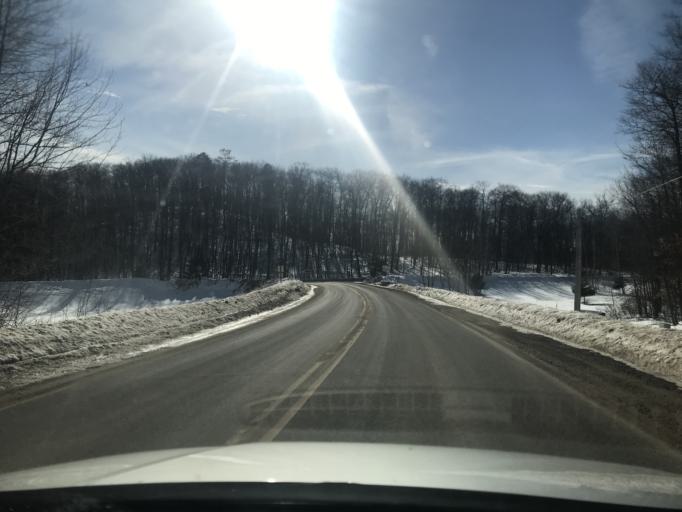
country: US
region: Michigan
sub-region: Dickinson County
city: Kingsford
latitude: 45.3971
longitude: -88.3419
